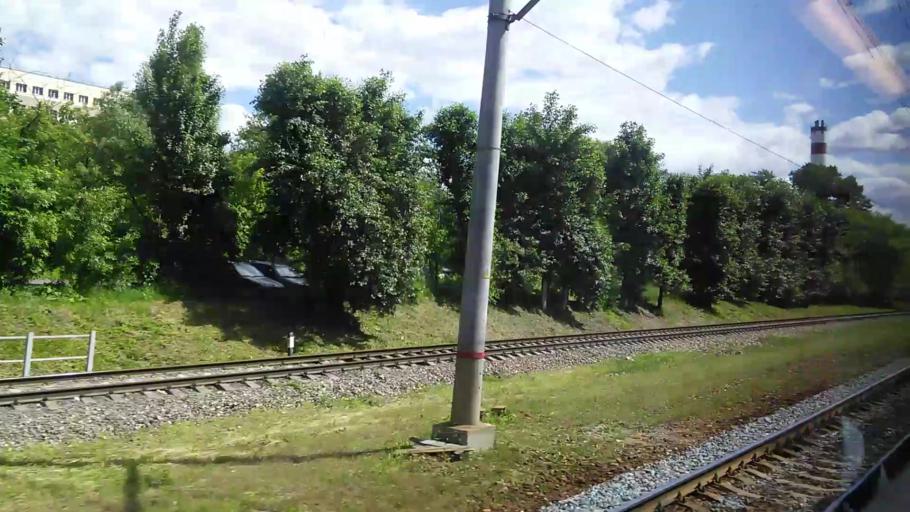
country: RU
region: Moscow
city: Slobodka
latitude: 55.8646
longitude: 37.5737
